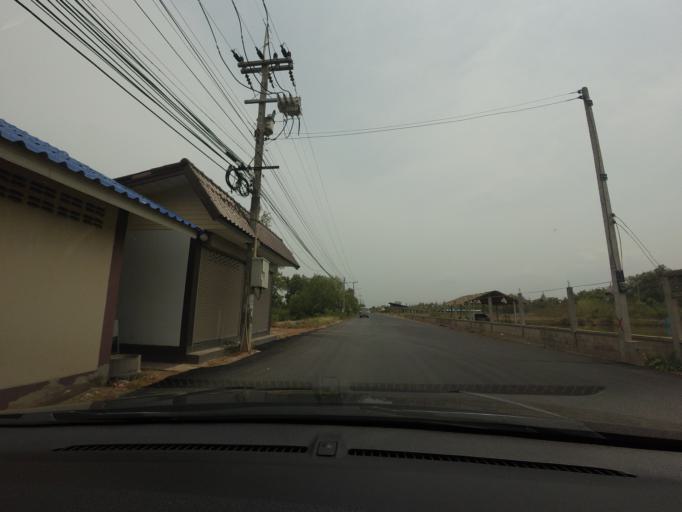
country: TH
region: Samut Songkhram
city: Amphawa
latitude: 13.3516
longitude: 99.9329
